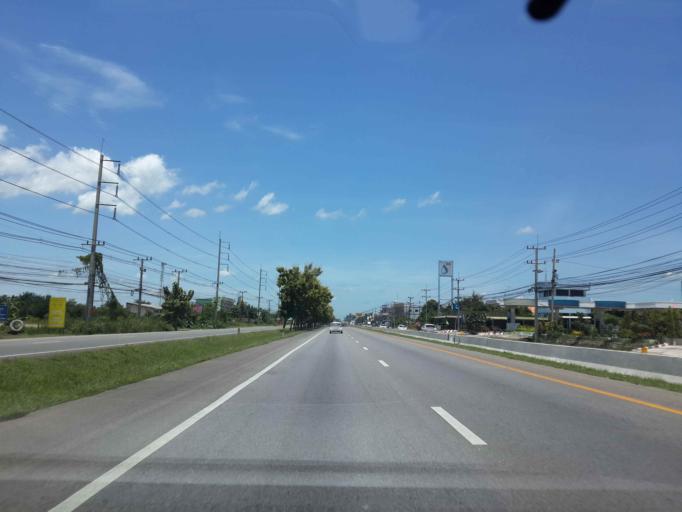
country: TH
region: Phetchaburi
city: Khao Yoi
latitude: 13.2902
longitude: 99.8221
